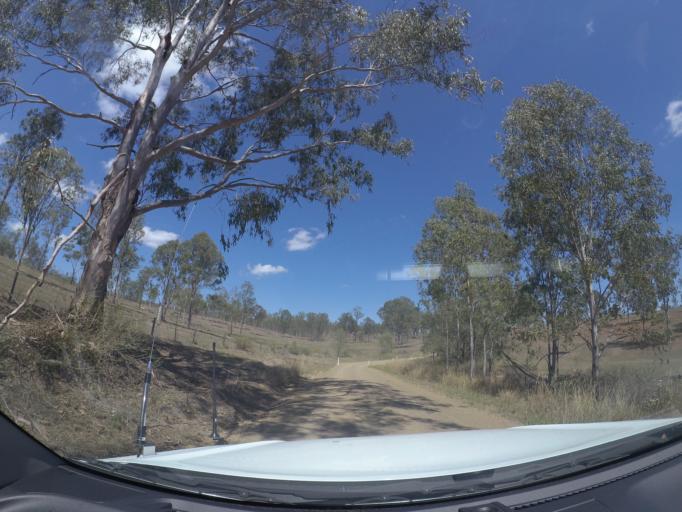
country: AU
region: Queensland
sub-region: Logan
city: Cedar Vale
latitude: -27.8567
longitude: 152.8829
